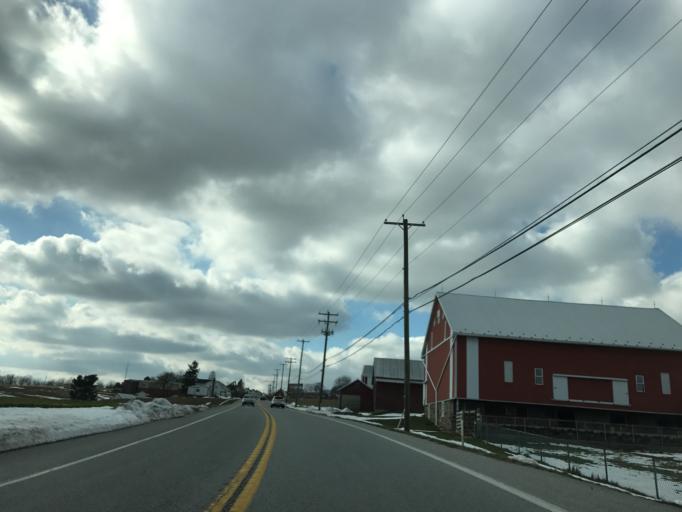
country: US
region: Pennsylvania
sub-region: York County
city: Parkville
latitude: 39.7363
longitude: -76.9292
